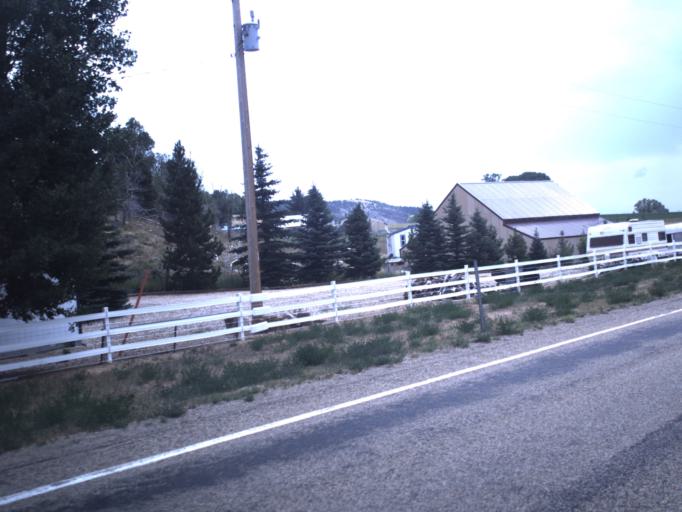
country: US
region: Utah
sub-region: Summit County
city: Francis
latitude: 40.4514
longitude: -110.8184
